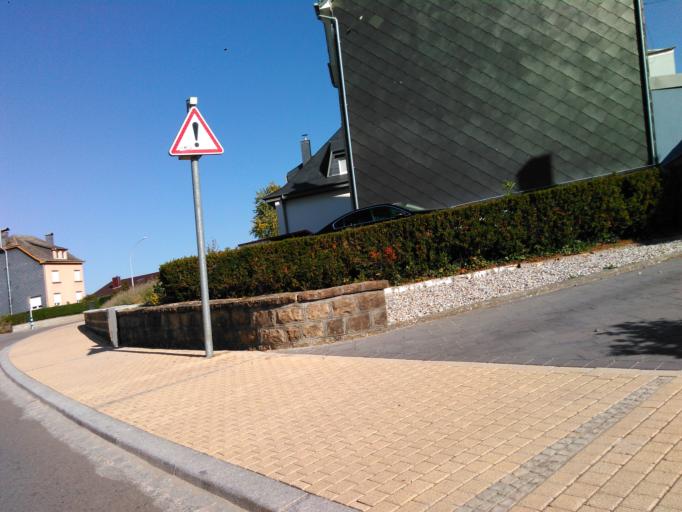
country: LU
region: Luxembourg
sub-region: Canton de Capellen
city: Steinfort
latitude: 49.6475
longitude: 5.9167
